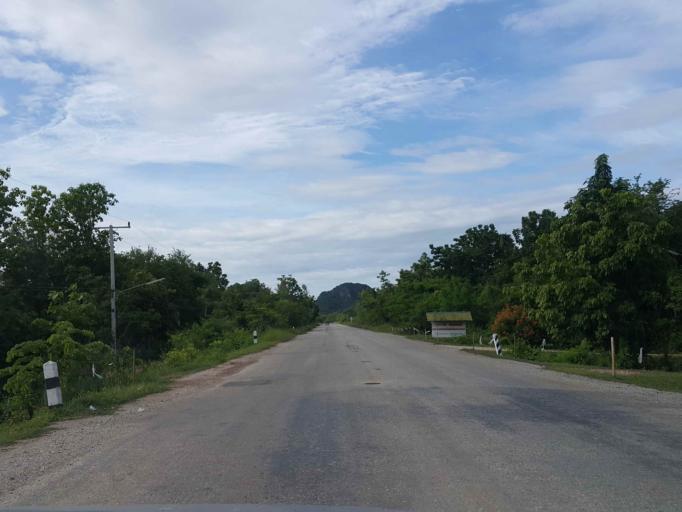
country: TH
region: Sukhothai
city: Thung Saliam
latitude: 17.3017
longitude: 99.5271
